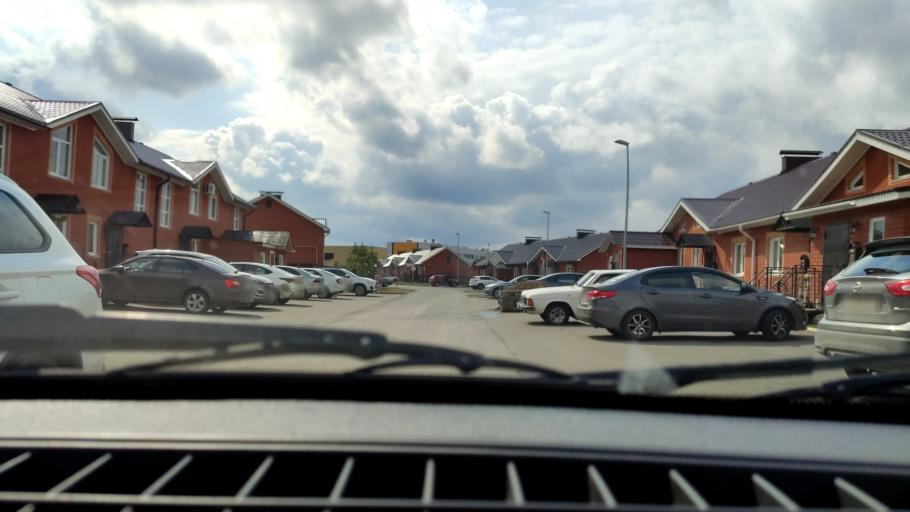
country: RU
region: Bashkortostan
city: Ufa
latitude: 54.5952
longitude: 55.9180
